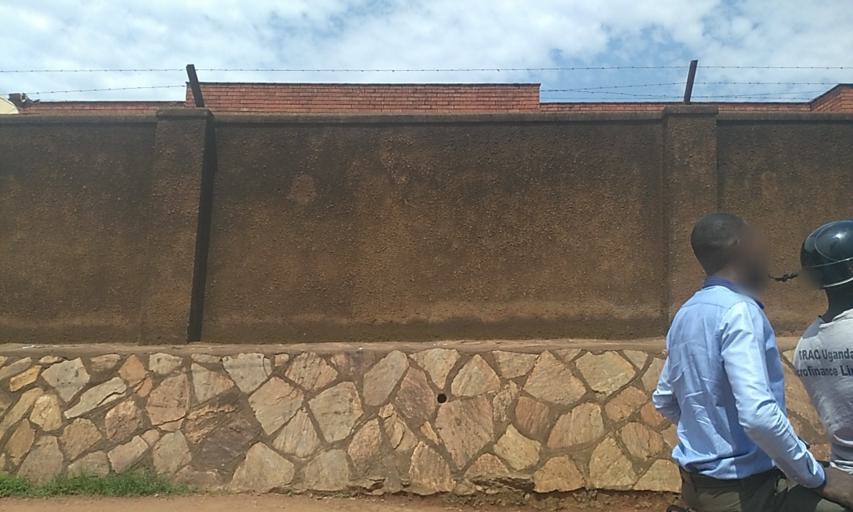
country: UG
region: Central Region
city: Kampala Central Division
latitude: 0.3116
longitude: 32.5657
